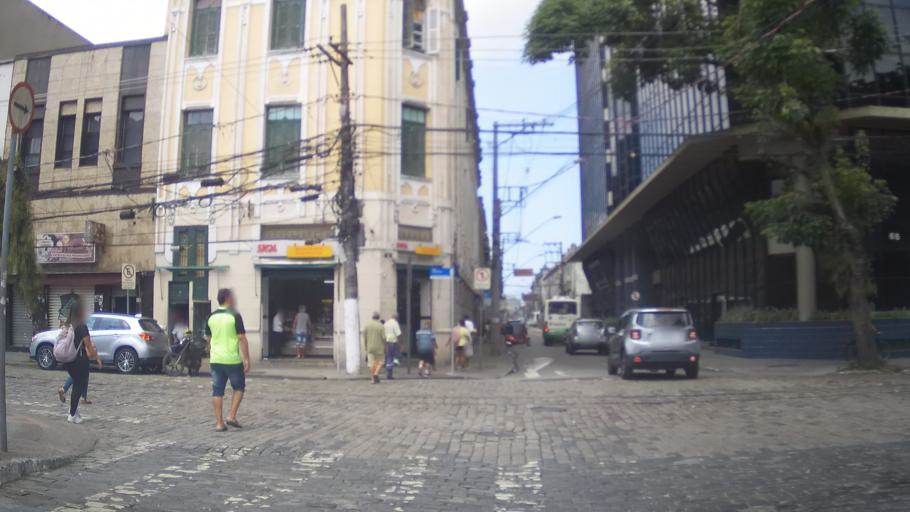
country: BR
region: Sao Paulo
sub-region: Santos
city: Santos
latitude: -23.9329
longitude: -46.3253
